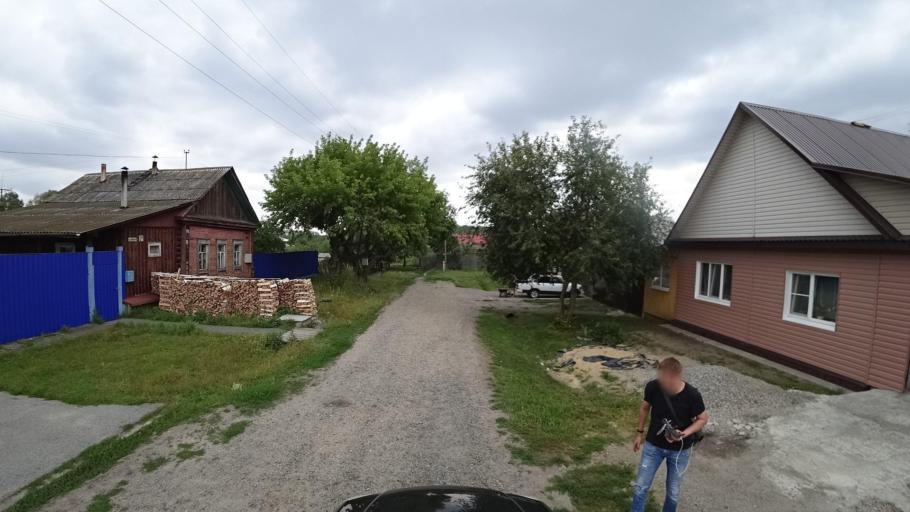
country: RU
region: Sverdlovsk
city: Kamyshlov
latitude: 56.8499
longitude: 62.6813
